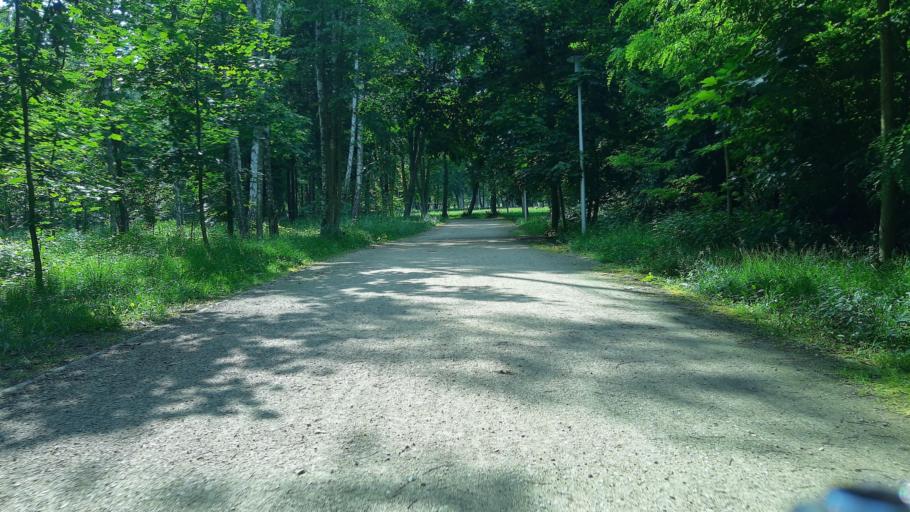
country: PL
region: Lodz Voivodeship
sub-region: Powiat sieradzki
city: Sieradz
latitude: 51.5972
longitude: 18.7556
